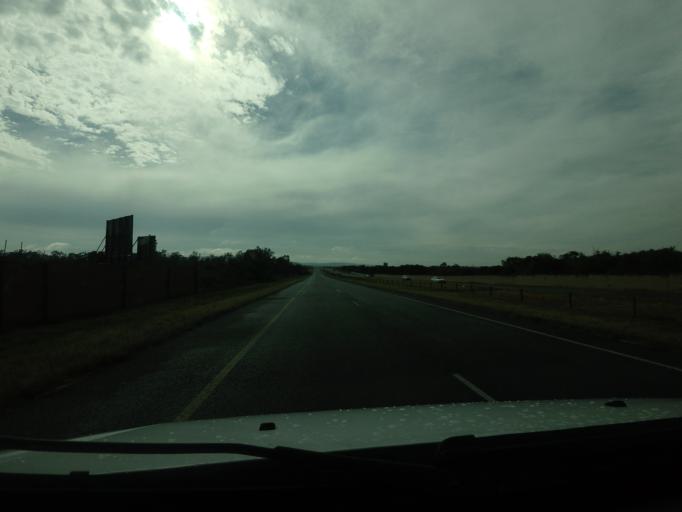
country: ZA
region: Gauteng
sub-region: City of Tshwane Metropolitan Municipality
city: Cullinan
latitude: -25.7640
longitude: 28.3835
